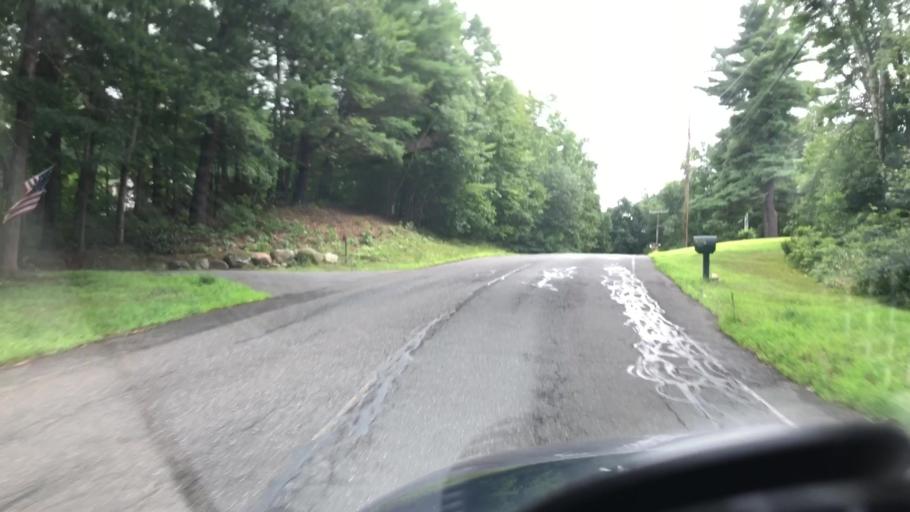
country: US
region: Massachusetts
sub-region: Hampshire County
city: Easthampton
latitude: 42.2460
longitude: -72.6943
